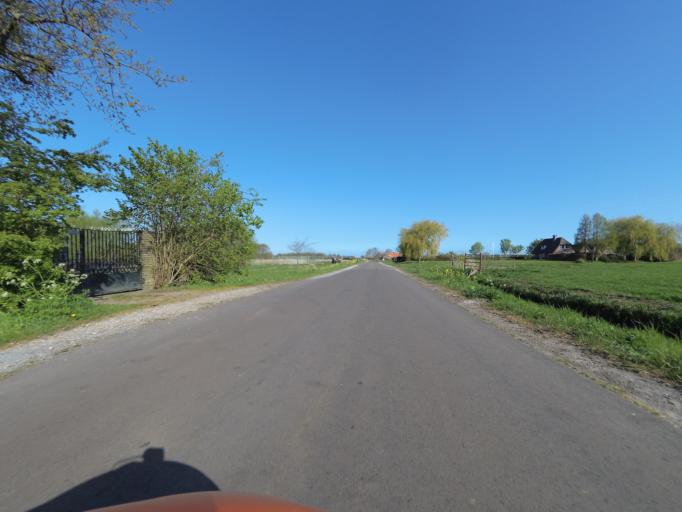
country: NL
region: North Holland
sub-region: Gemeente Naarden
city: Naarden
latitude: 52.3036
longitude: 5.1261
